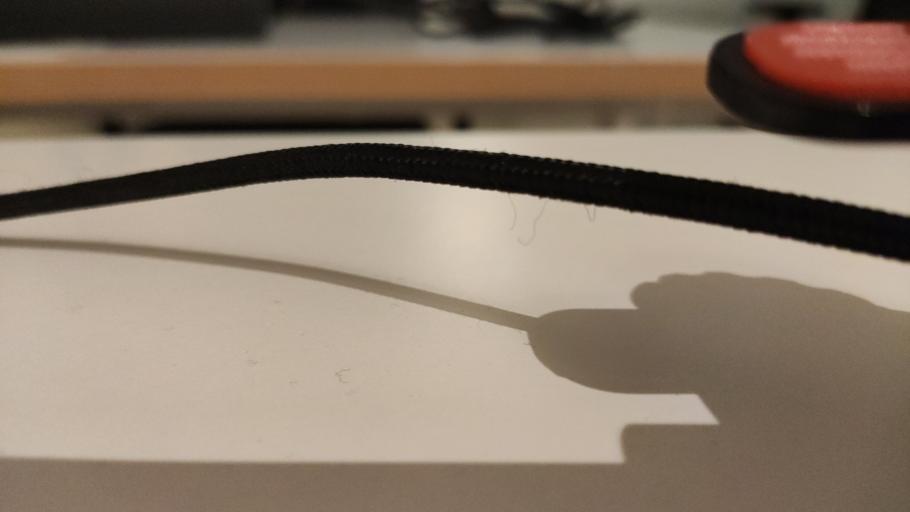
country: RU
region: Moskovskaya
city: Bogorodskoye
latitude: 56.4409
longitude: 37.9021
